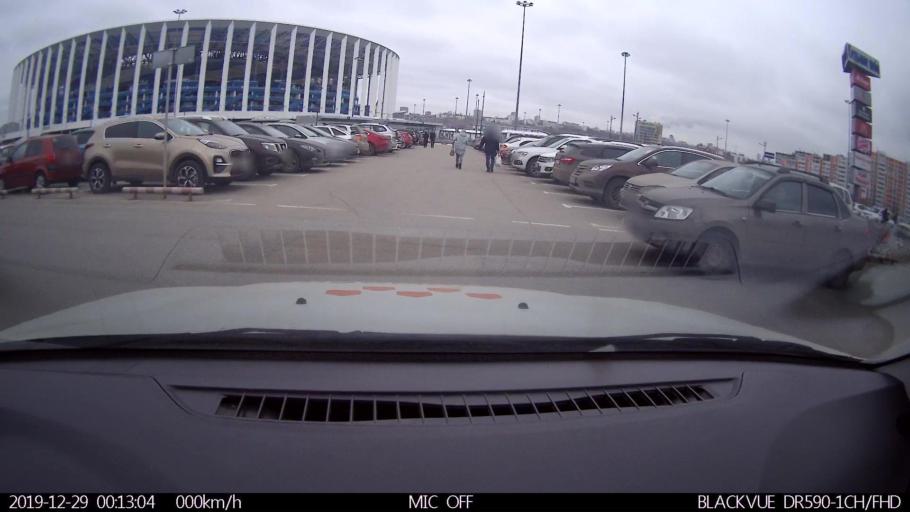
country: RU
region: Nizjnij Novgorod
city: Nizhniy Novgorod
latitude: 56.3386
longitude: 43.9573
